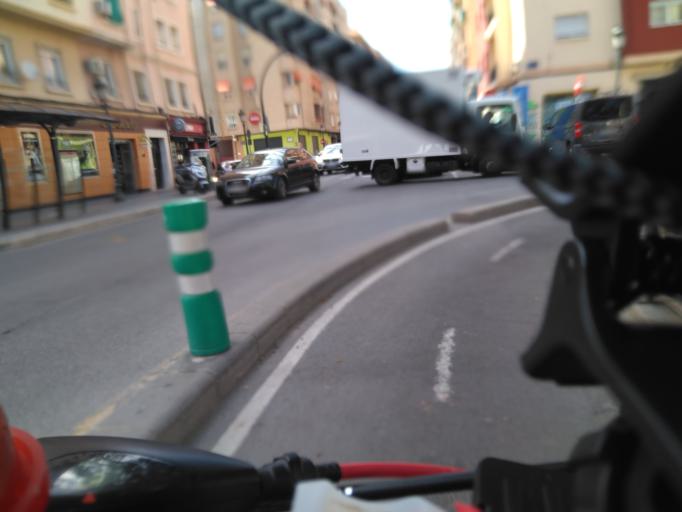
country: ES
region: Valencia
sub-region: Provincia de Valencia
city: Valencia
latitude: 39.4701
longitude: -0.3947
